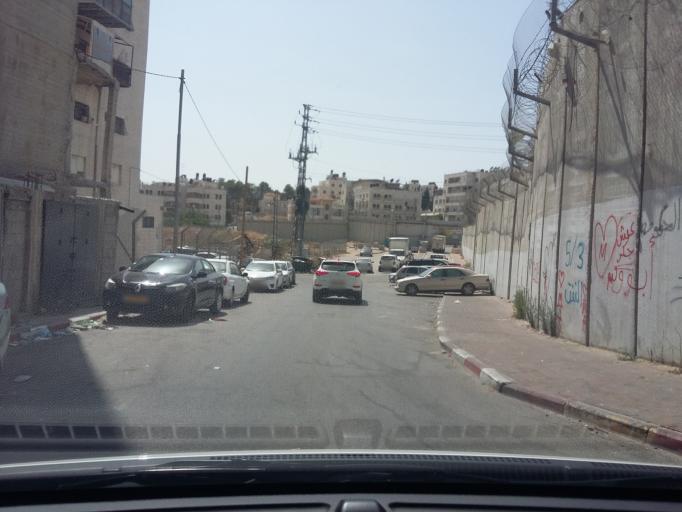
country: PS
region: West Bank
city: Ar Ram wa Dahiyat al Barid
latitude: 31.8447
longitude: 35.2307
